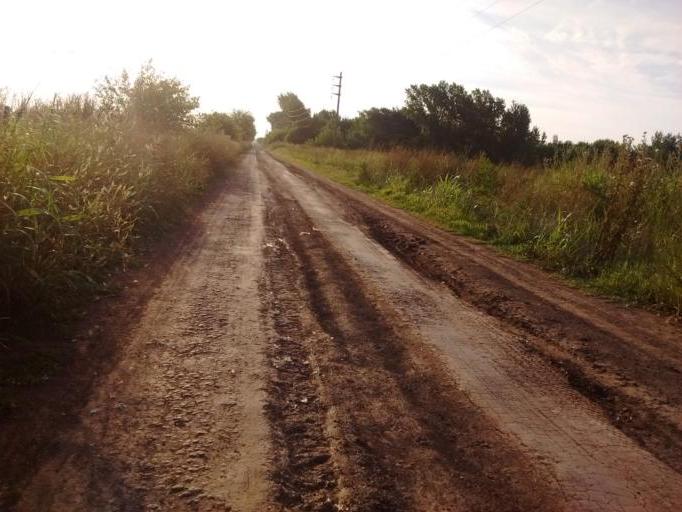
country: AR
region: Santa Fe
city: Funes
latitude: -32.9309
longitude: -60.8621
